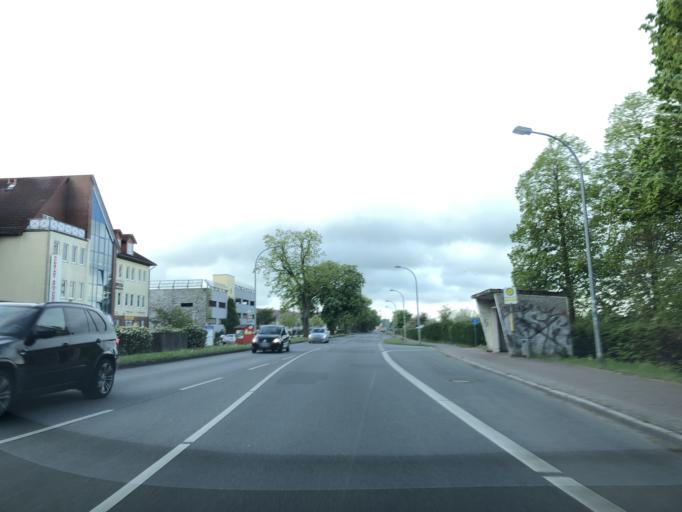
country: DE
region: Mecklenburg-Vorpommern
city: Guestrow
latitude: 53.7808
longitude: 12.1758
